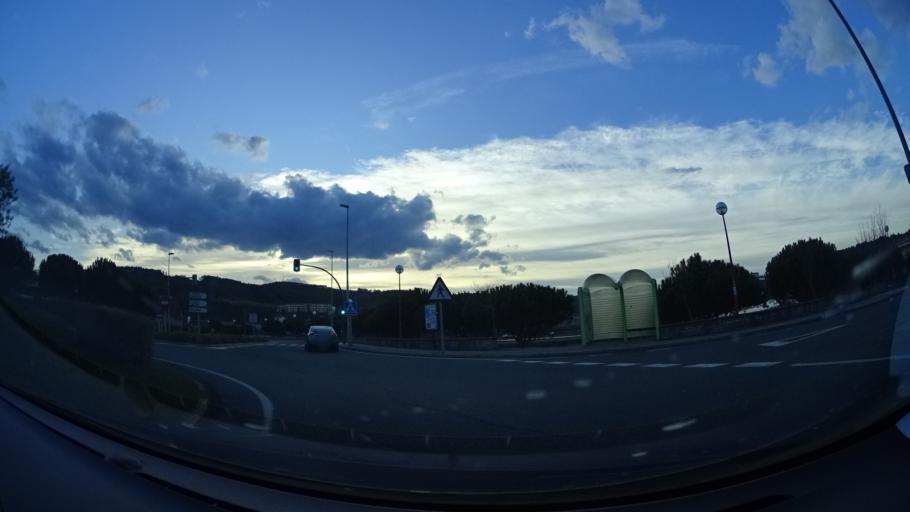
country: ES
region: Basque Country
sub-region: Bizkaia
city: Plentzia
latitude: 43.4018
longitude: -2.9428
